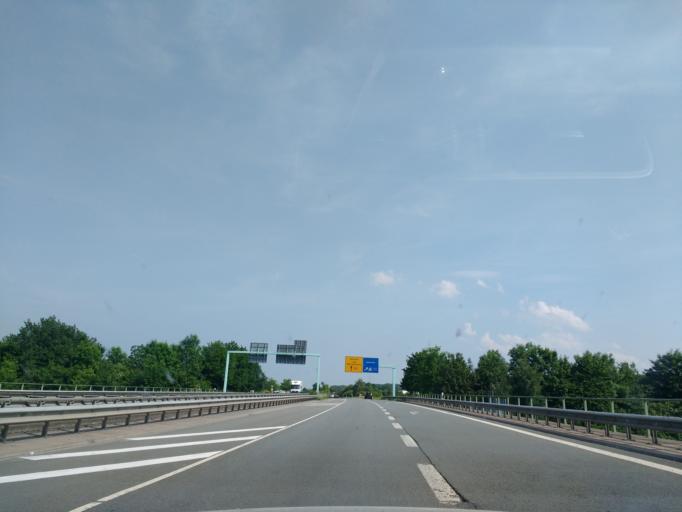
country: DE
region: North Rhine-Westphalia
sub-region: Regierungsbezirk Detmold
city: Herford
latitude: 52.0892
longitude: 8.6957
